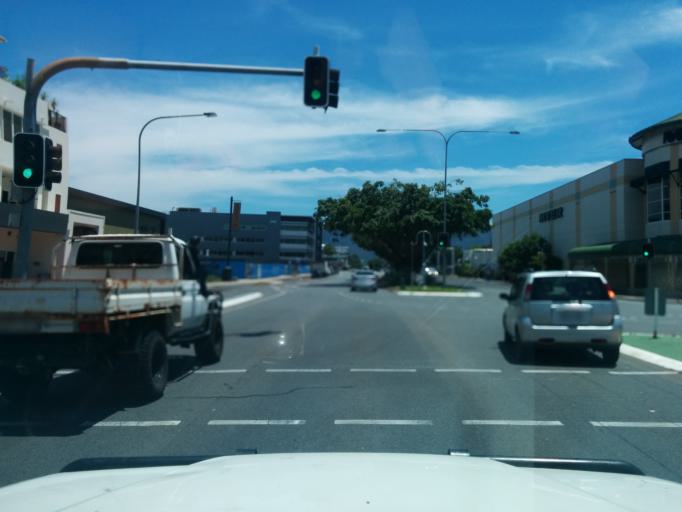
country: AU
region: Queensland
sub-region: Cairns
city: Cairns
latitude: -16.9261
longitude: 145.7744
